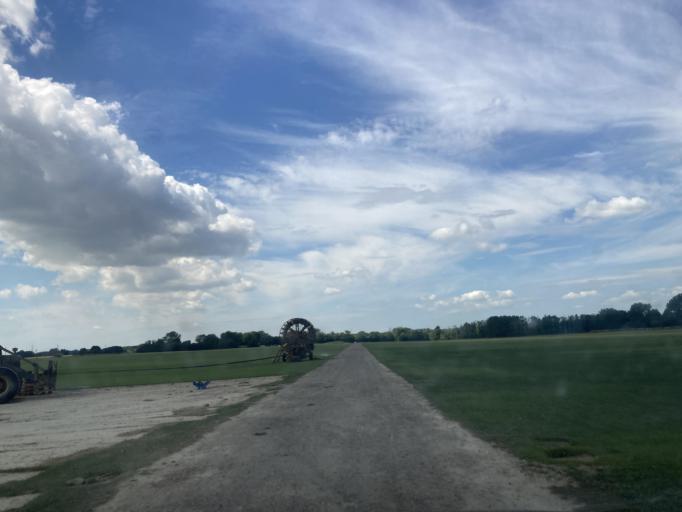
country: DK
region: Zealand
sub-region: Koge Kommune
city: Borup
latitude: 55.4601
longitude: 11.9631
